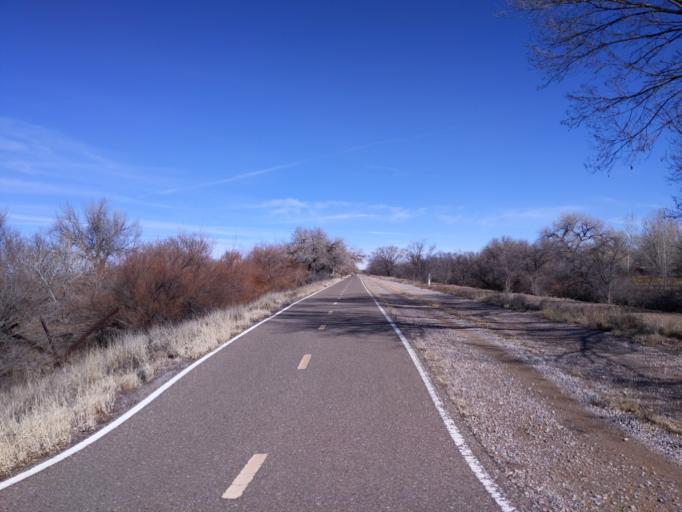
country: US
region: New Mexico
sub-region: Bernalillo County
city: Lee Acres
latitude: 35.1520
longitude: -106.6701
